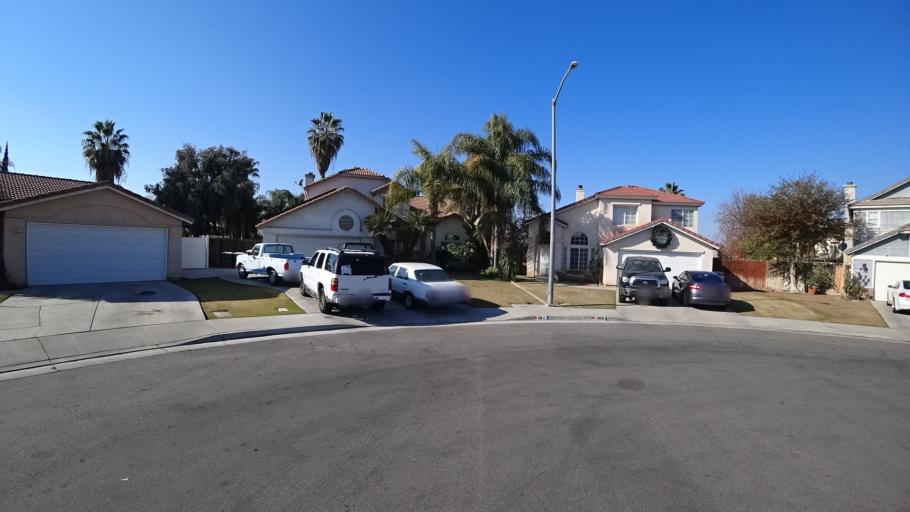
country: US
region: California
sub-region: Kern County
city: Greenfield
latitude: 35.2937
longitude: -119.0462
